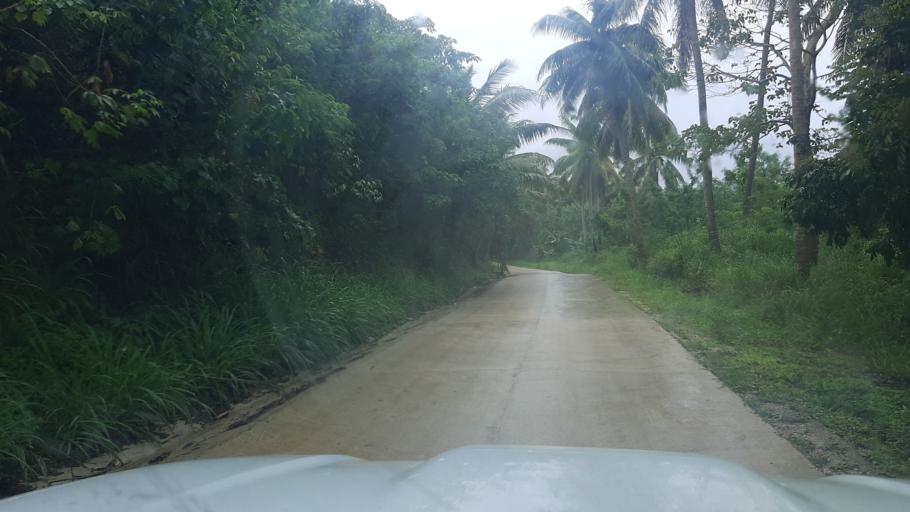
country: VU
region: Shefa
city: Port-Vila
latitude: -17.6366
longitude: 168.2076
